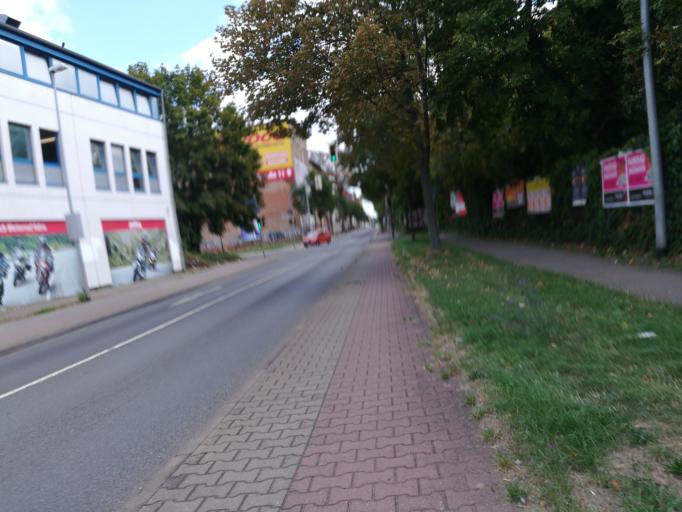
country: DE
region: Saxony-Anhalt
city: Neue Neustadt
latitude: 52.1528
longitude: 11.6320
